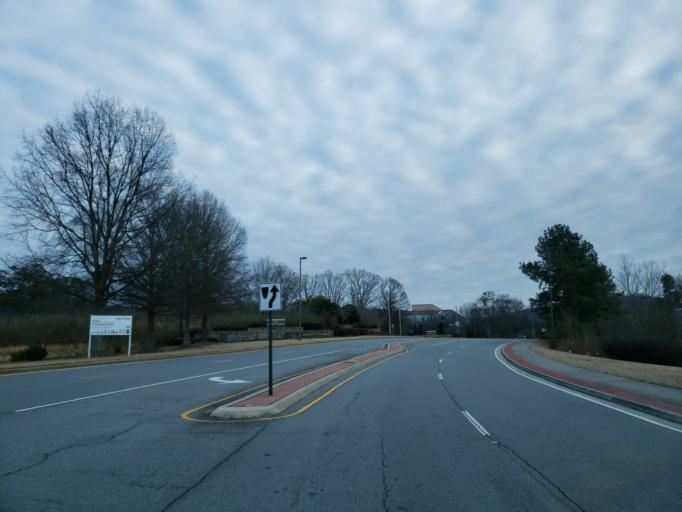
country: US
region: Georgia
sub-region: Cobb County
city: Kennesaw
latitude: 34.0008
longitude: -84.5810
